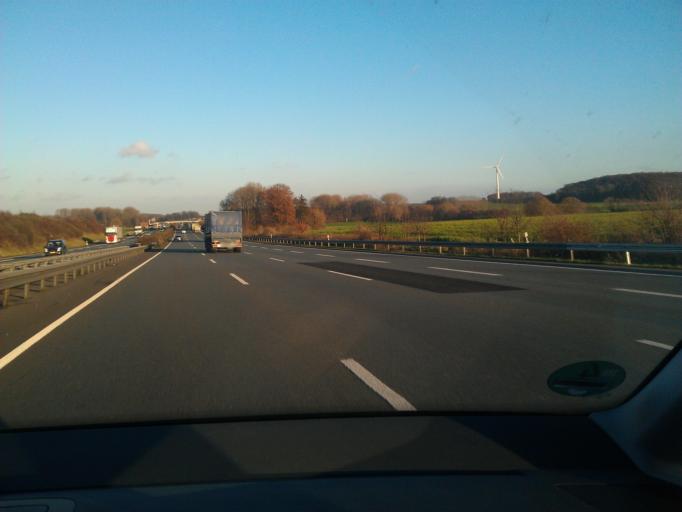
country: DE
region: North Rhine-Westphalia
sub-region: Regierungsbezirk Munster
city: Beckum
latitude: 51.7928
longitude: 8.0770
